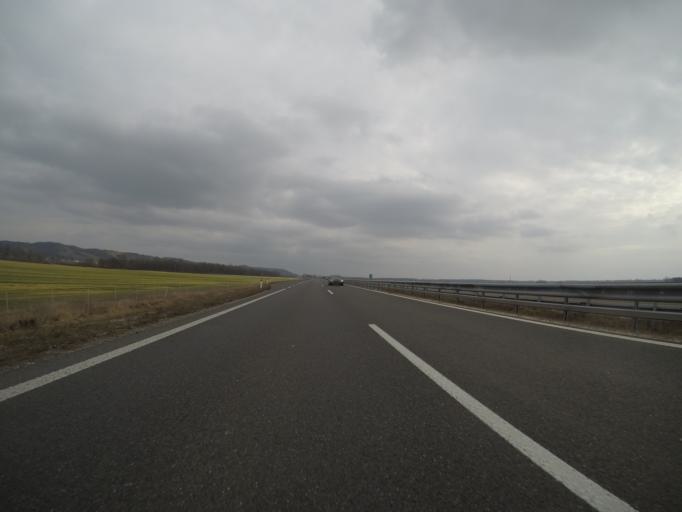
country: HR
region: Medimurska
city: Peklenica
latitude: 46.5314
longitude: 16.4850
